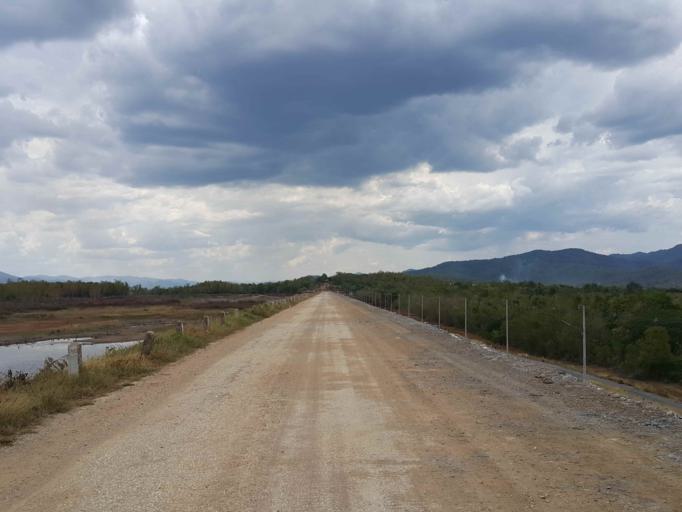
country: TH
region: Sukhothai
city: Thung Saliam
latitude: 17.3168
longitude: 99.4242
